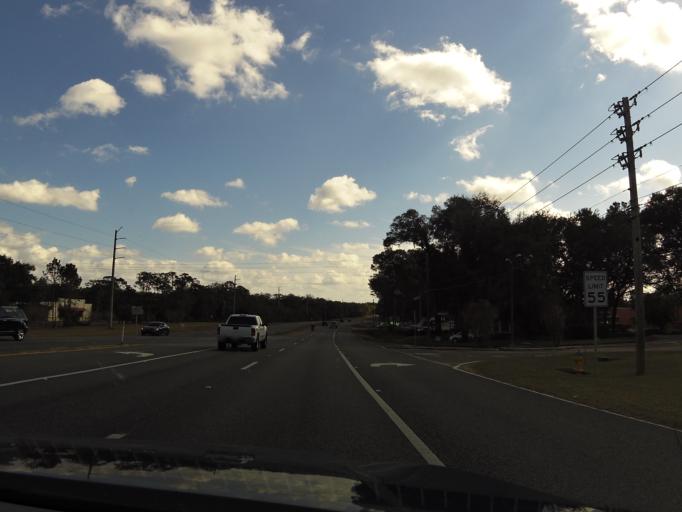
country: US
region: Florida
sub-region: Volusia County
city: De Leon Springs
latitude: 29.0872
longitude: -81.3239
